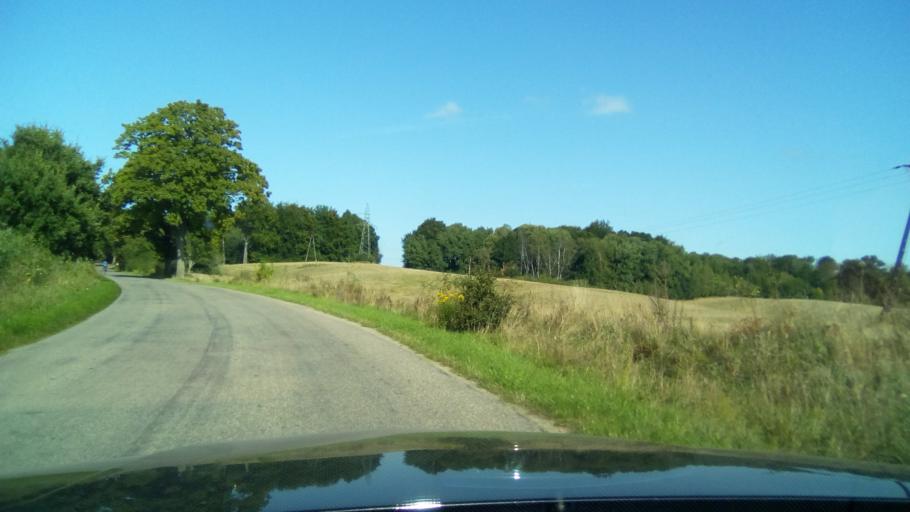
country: PL
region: West Pomeranian Voivodeship
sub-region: Powiat szczecinecki
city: Borne Sulinowo
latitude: 53.6411
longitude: 16.4902
